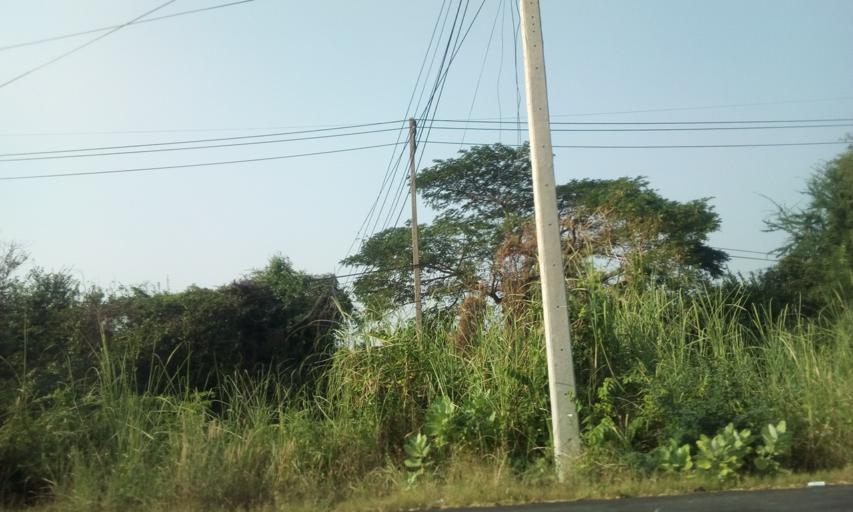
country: TH
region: Sing Buri
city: Phrom Buri
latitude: 14.7600
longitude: 100.4347
